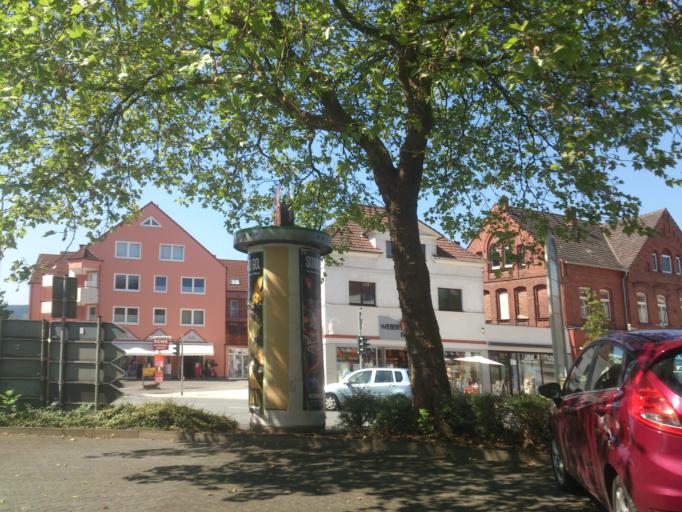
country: DE
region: North Rhine-Westphalia
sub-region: Regierungsbezirk Detmold
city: Bad Driburg
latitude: 51.7343
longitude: 9.0238
